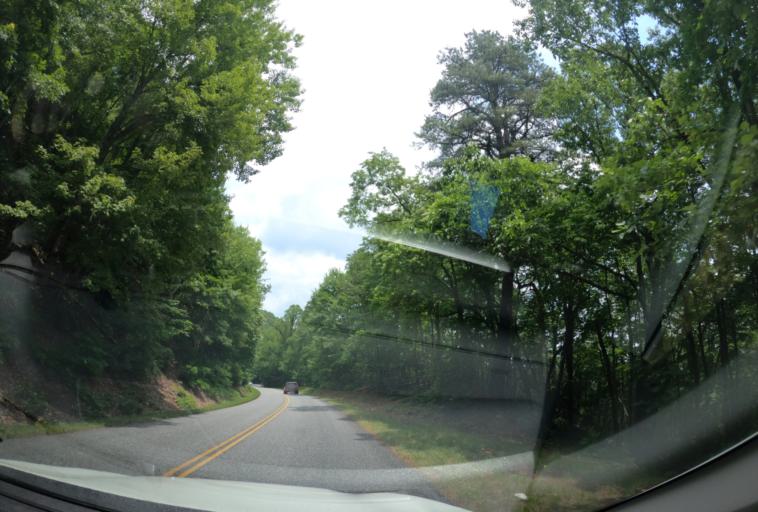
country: US
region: North Carolina
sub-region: Buncombe County
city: Avery Creek
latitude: 35.4668
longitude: -82.6269
